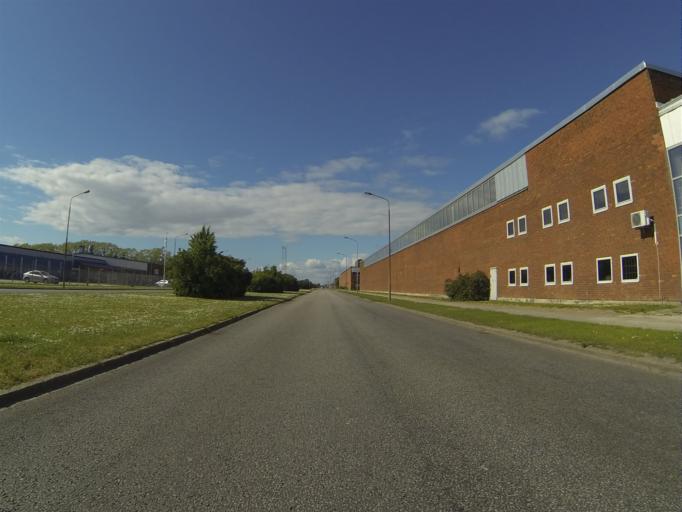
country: SE
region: Skane
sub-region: Burlovs Kommun
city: Arloev
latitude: 55.6209
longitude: 13.0386
